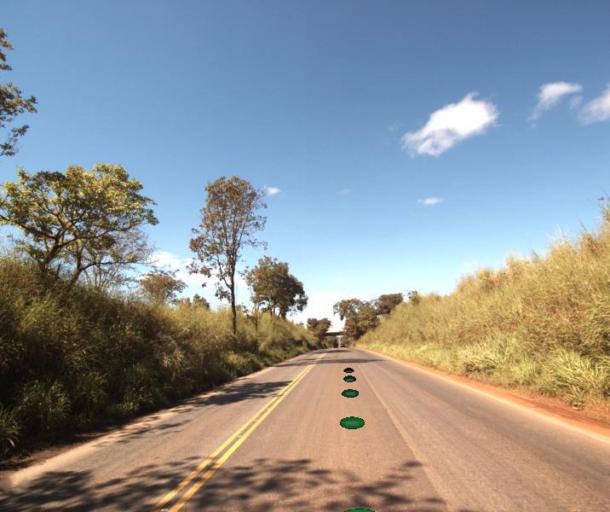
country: BR
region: Goias
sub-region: Rialma
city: Rialma
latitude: -15.3182
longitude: -49.5723
